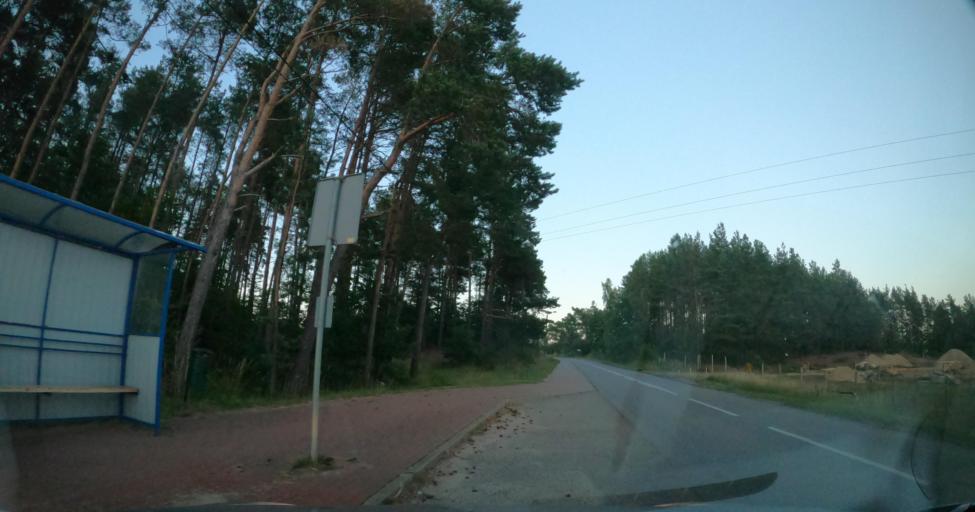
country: PL
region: Pomeranian Voivodeship
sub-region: Powiat wejherowski
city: Linia
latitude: 54.4573
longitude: 18.0092
